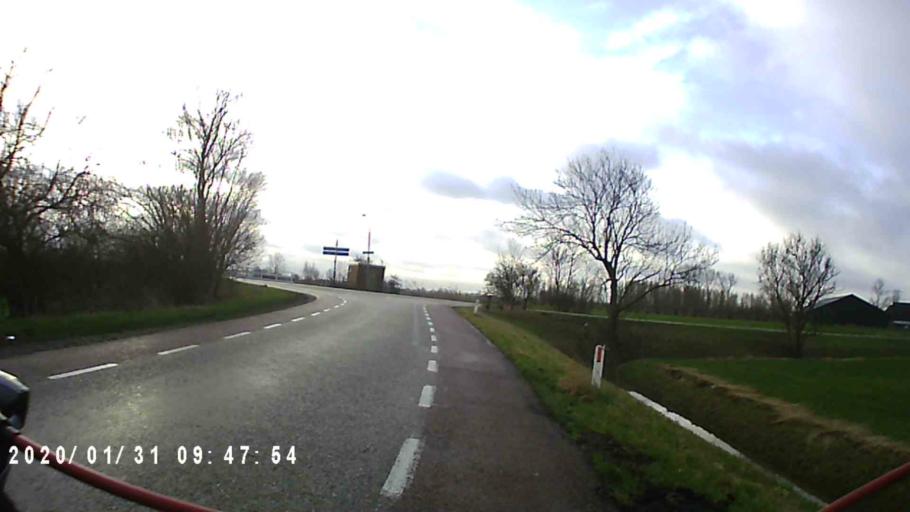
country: NL
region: Groningen
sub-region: Gemeente Zuidhorn
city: Aduard
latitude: 53.2621
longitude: 6.4818
